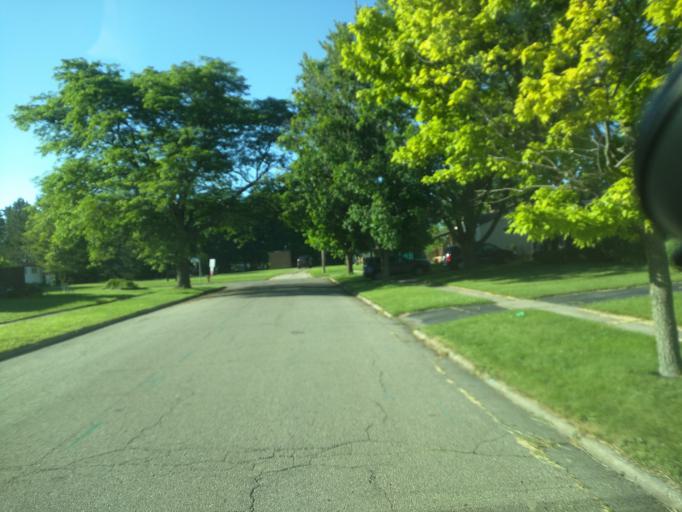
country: US
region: Michigan
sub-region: Ingham County
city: Edgemont Park
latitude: 42.7457
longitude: -84.5933
